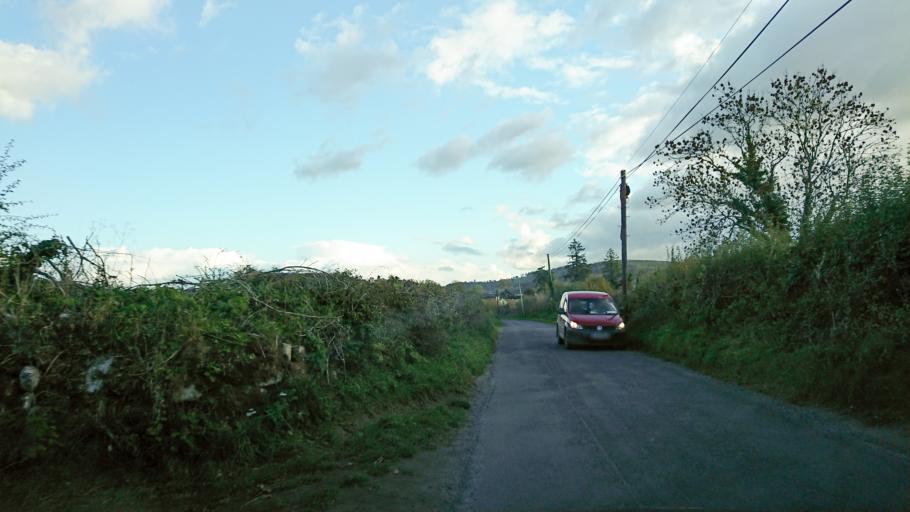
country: IE
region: Leinster
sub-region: Kilkenny
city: Graiguenamanagh
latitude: 52.4760
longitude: -6.9121
